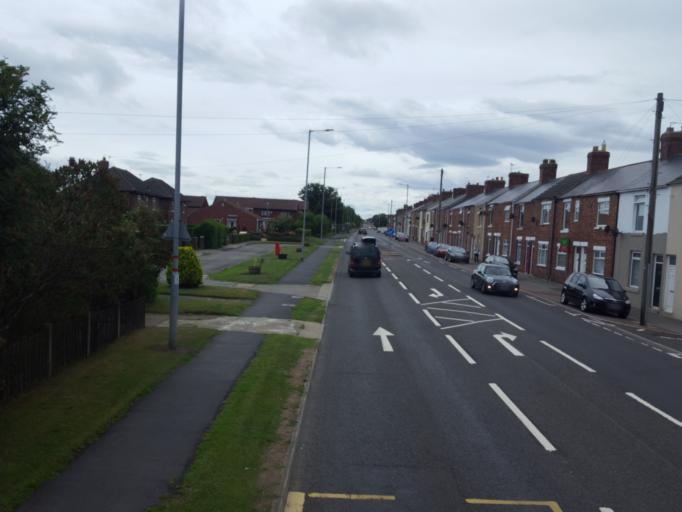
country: GB
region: England
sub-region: County Durham
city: Durham
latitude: 54.8040
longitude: -1.5884
